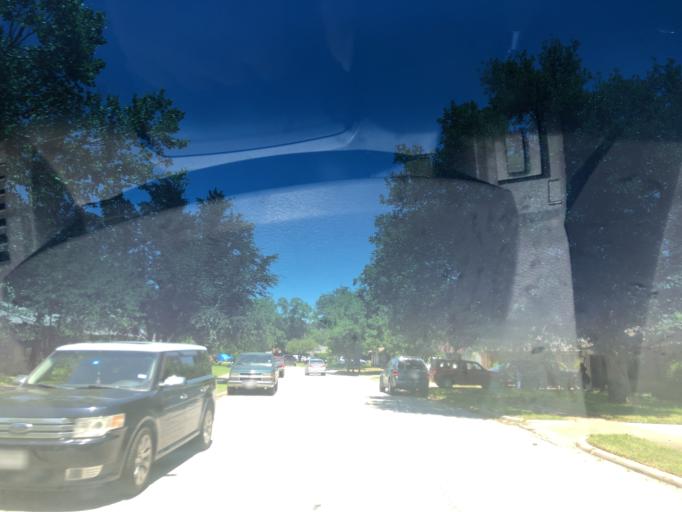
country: US
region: Texas
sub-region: Dallas County
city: Grand Prairie
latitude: 32.7182
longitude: -97.0105
